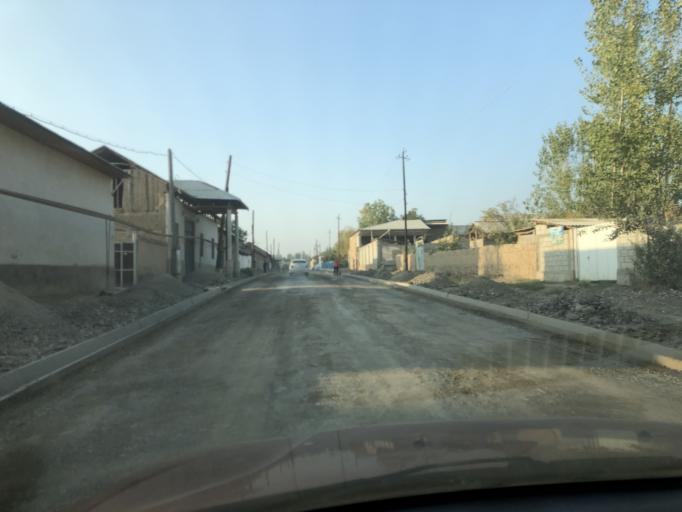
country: UZ
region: Namangan
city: Uychi
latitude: 41.0812
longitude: 72.0000
